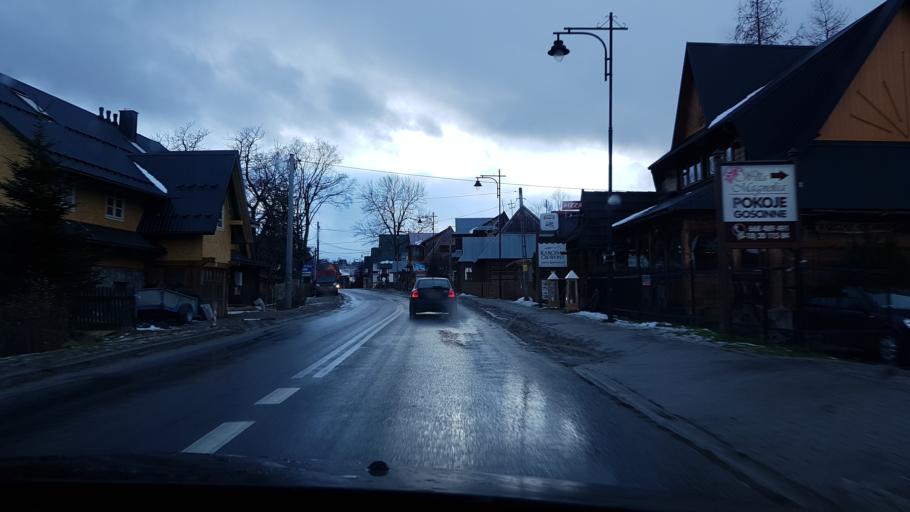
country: PL
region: Lesser Poland Voivodeship
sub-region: Powiat tatrzanski
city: Bukowina Tatrzanska
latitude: 49.3406
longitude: 20.1032
